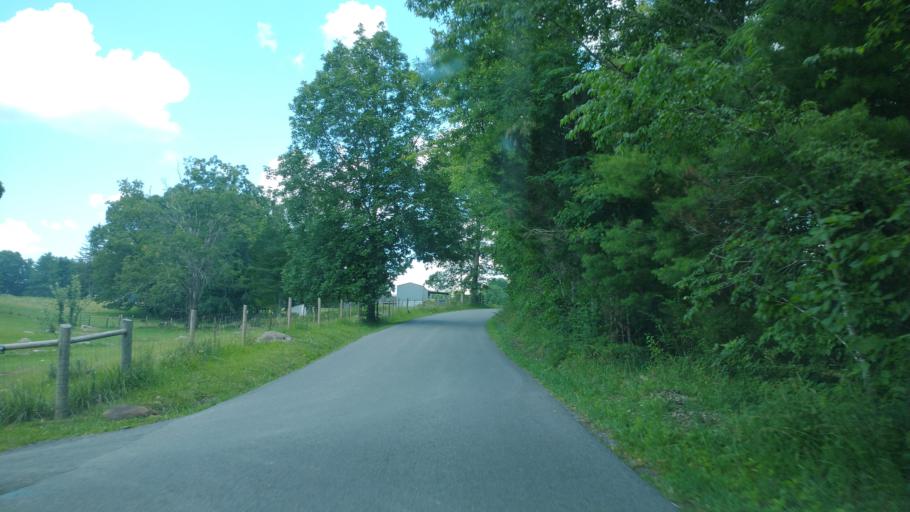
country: US
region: West Virginia
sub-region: Mercer County
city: Athens
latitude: 37.4573
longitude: -81.0361
